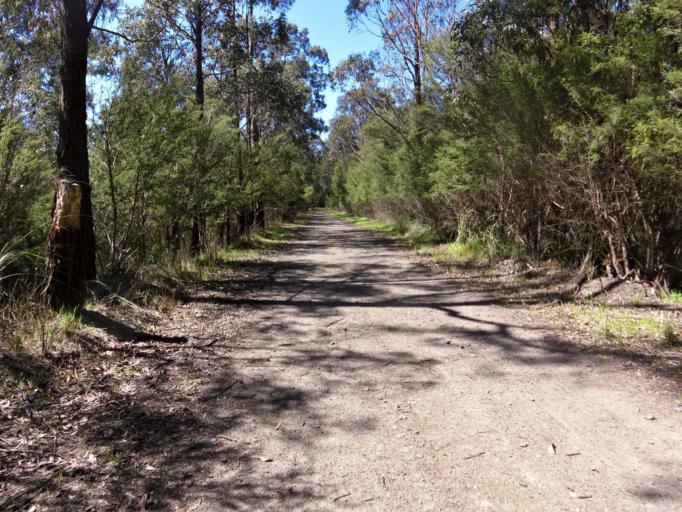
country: AU
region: Victoria
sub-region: Latrobe
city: Moe
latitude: -38.1686
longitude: 146.3222
